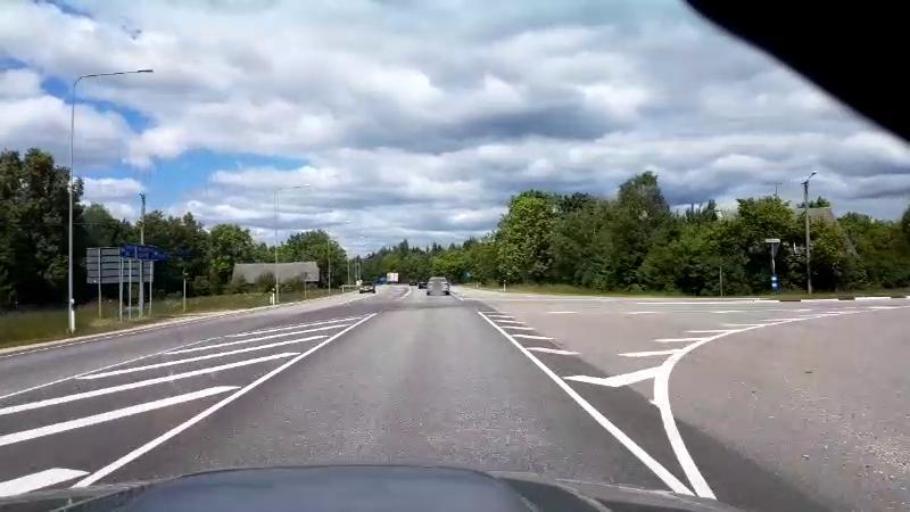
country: EE
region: Paernumaa
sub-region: Halinga vald
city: Parnu-Jaagupi
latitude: 58.6163
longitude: 24.5125
